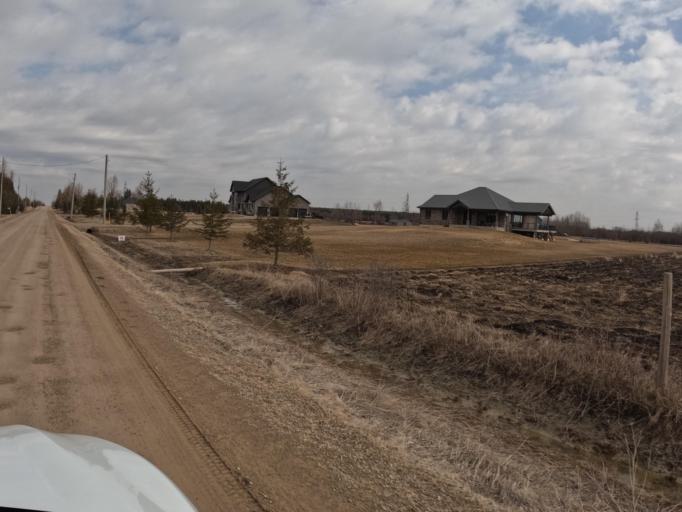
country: CA
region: Ontario
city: Orangeville
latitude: 43.9284
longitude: -80.2197
